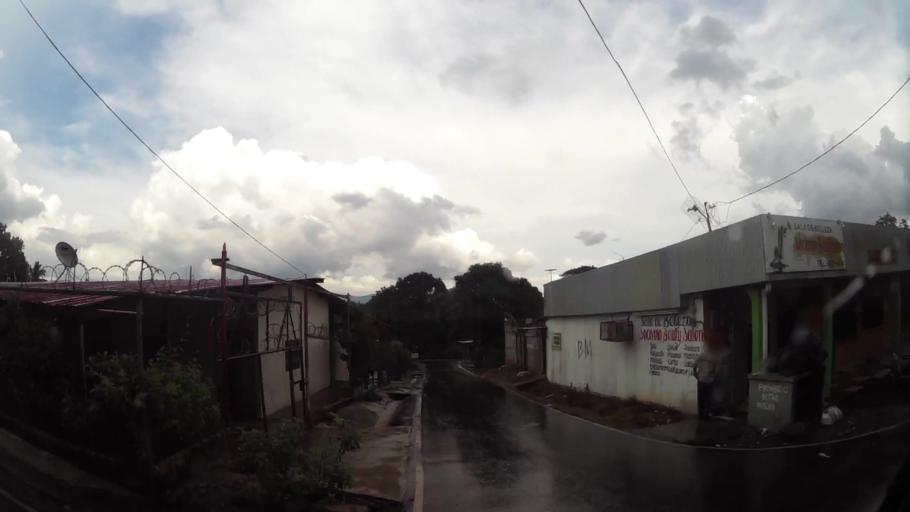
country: PA
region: Panama
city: Cabra Numero Uno
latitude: 9.1006
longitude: -79.3266
